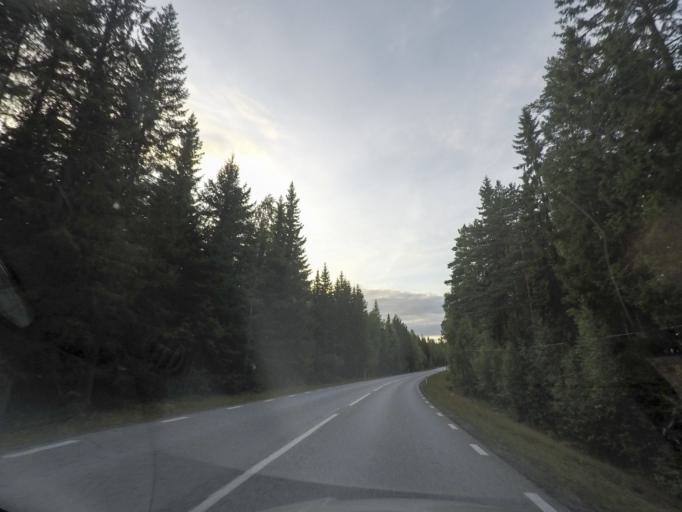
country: SE
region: OErebro
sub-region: Hallefors Kommun
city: Haellefors
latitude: 59.6125
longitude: 14.6438
